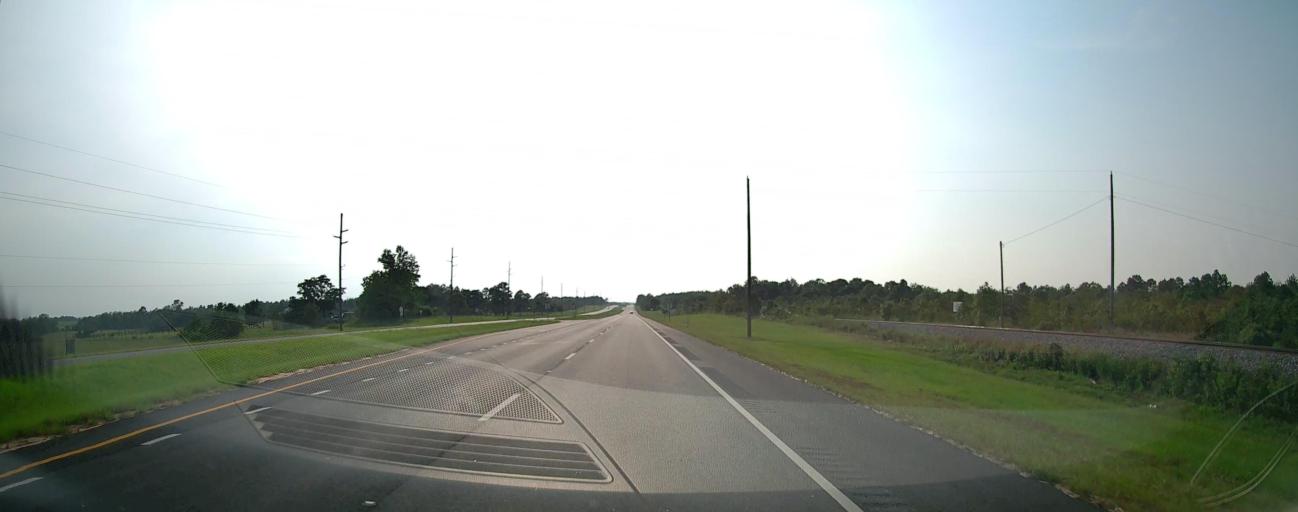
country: US
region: Georgia
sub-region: Taylor County
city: Butler
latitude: 32.5839
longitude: -84.3352
